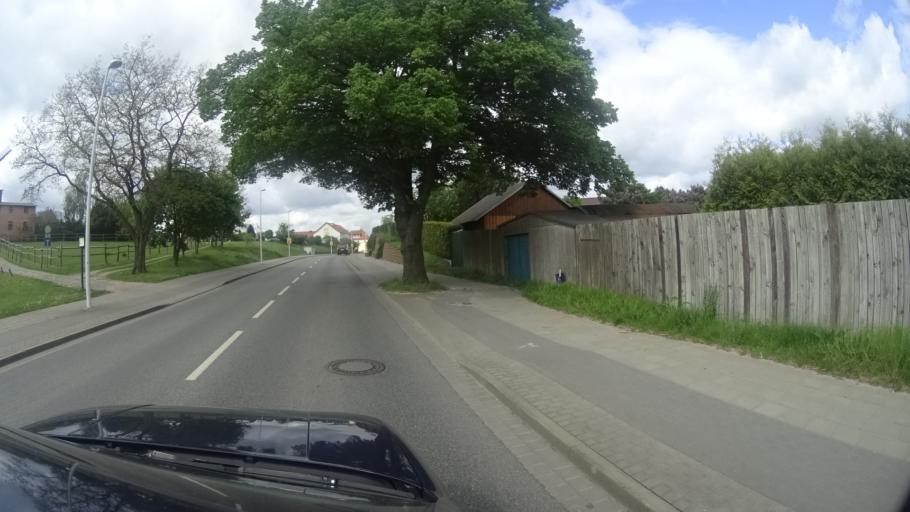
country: DE
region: Mecklenburg-Vorpommern
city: Malchow
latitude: 53.4790
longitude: 12.4224
